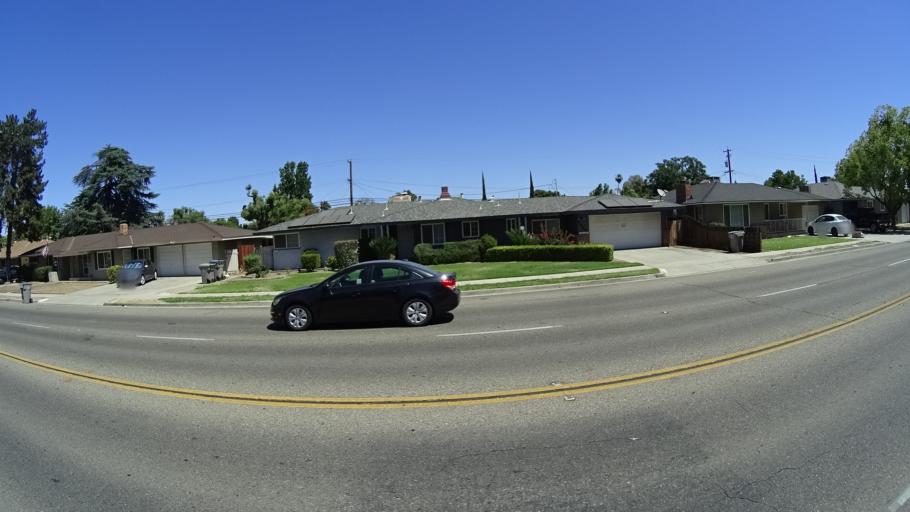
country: US
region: California
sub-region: Fresno County
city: Fresno
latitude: 36.7722
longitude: -119.7422
